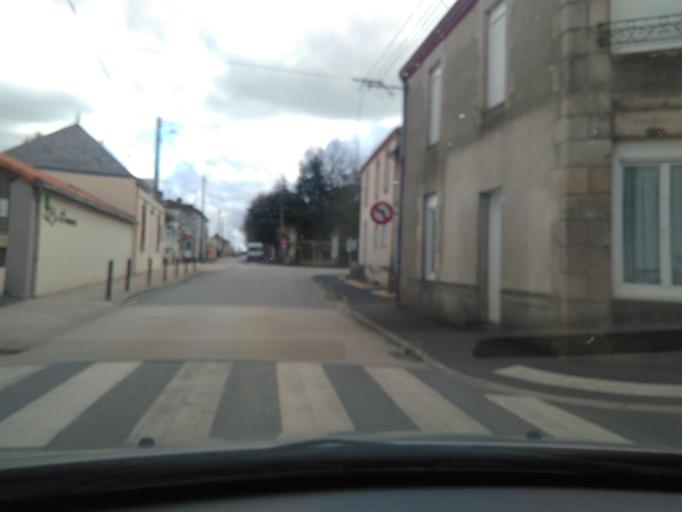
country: FR
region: Pays de la Loire
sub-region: Departement de la Vendee
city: Saint-Martin-des-Noyers
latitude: 46.7206
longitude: -1.1778
